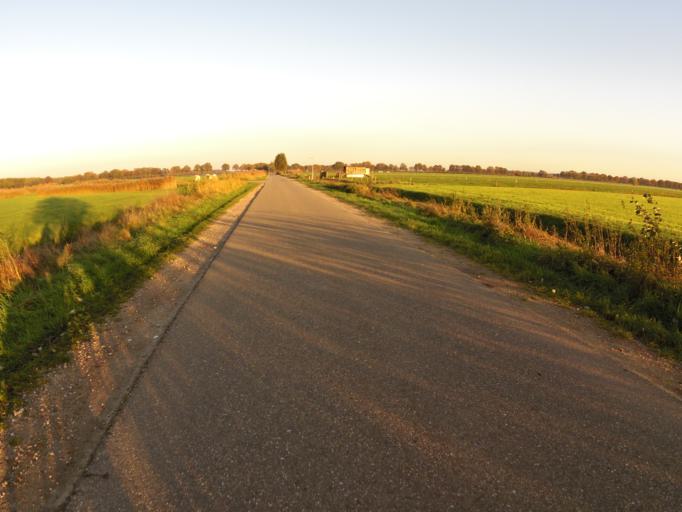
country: NL
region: North Brabant
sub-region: Gemeente Heusden
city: Heusden
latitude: 51.6802
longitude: 5.1654
